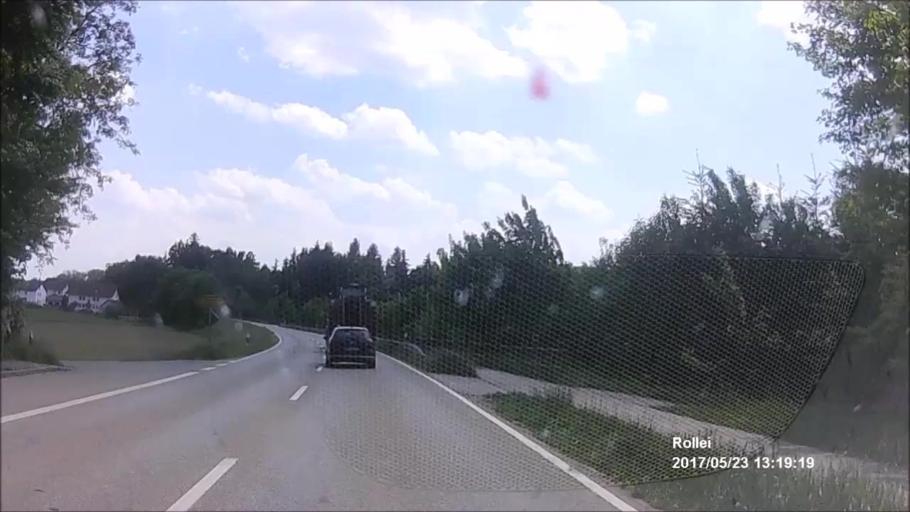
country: DE
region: Bavaria
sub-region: Upper Bavaria
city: Taufkirchen
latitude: 48.3598
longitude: 12.1250
